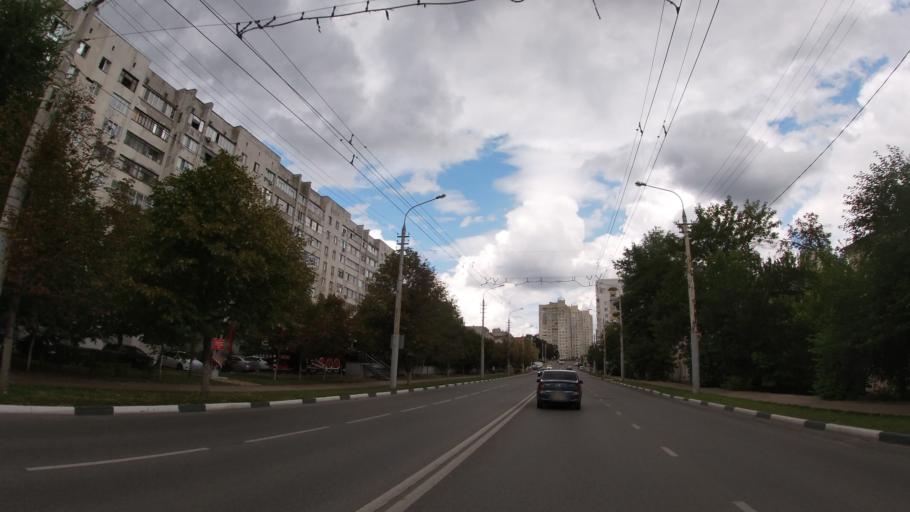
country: RU
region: Belgorod
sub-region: Belgorodskiy Rayon
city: Belgorod
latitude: 50.5967
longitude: 36.6063
